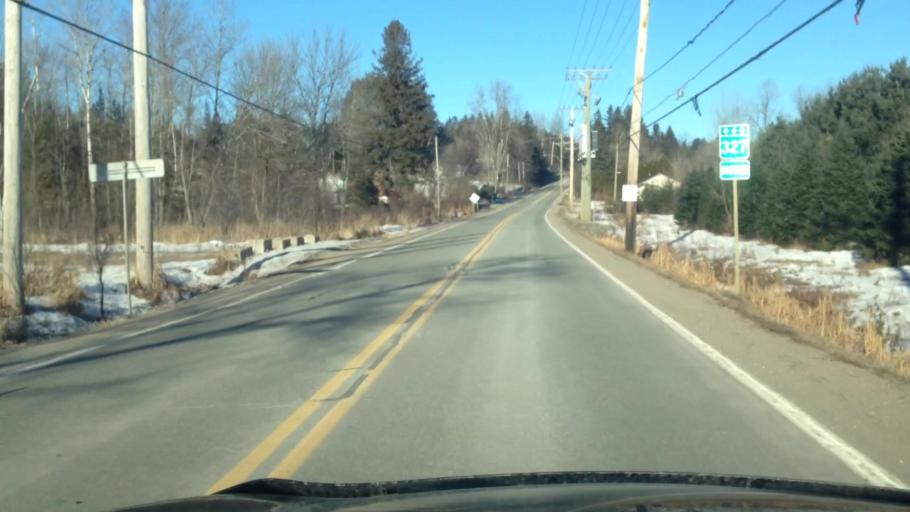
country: CA
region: Quebec
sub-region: Laurentides
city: Mont-Tremblant
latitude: 45.9731
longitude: -74.6149
